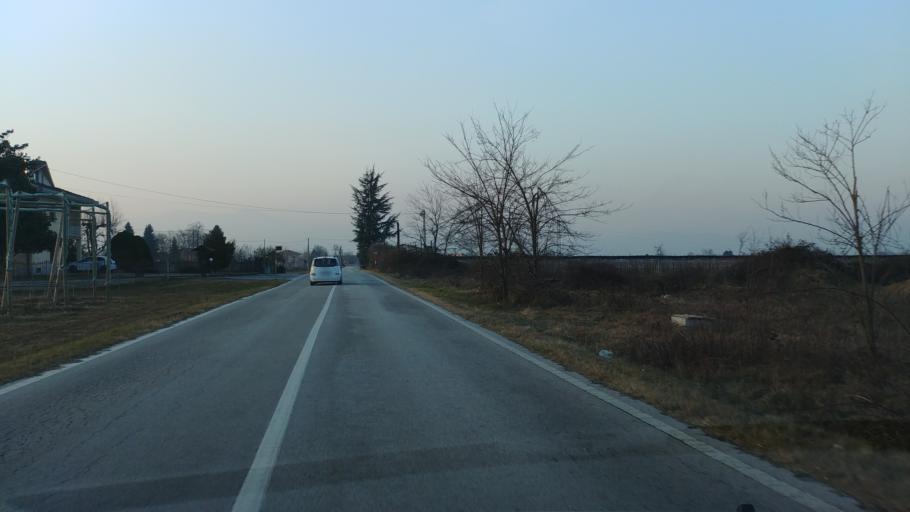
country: IT
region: Piedmont
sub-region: Provincia di Cuneo
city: Roata Rossi
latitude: 44.4205
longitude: 7.5317
